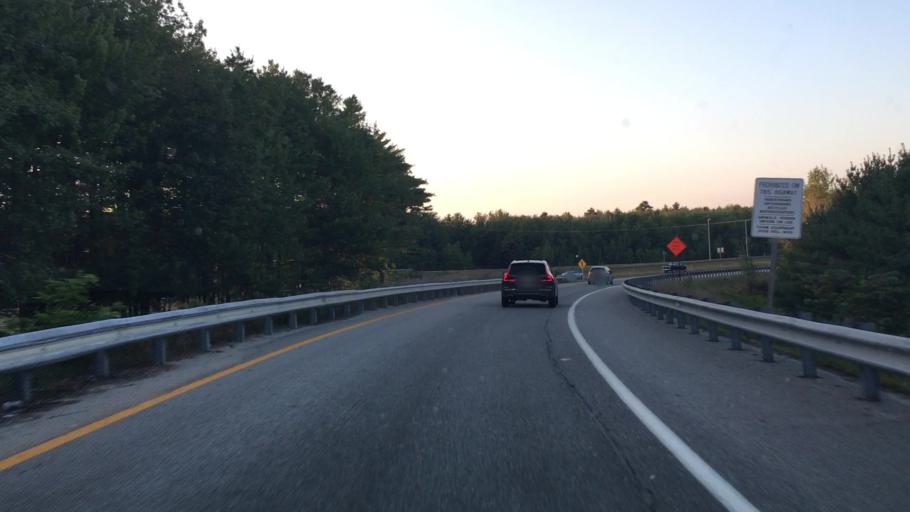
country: US
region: Maine
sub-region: Sagadahoc County
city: Topsham
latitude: 43.9417
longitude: -69.9774
